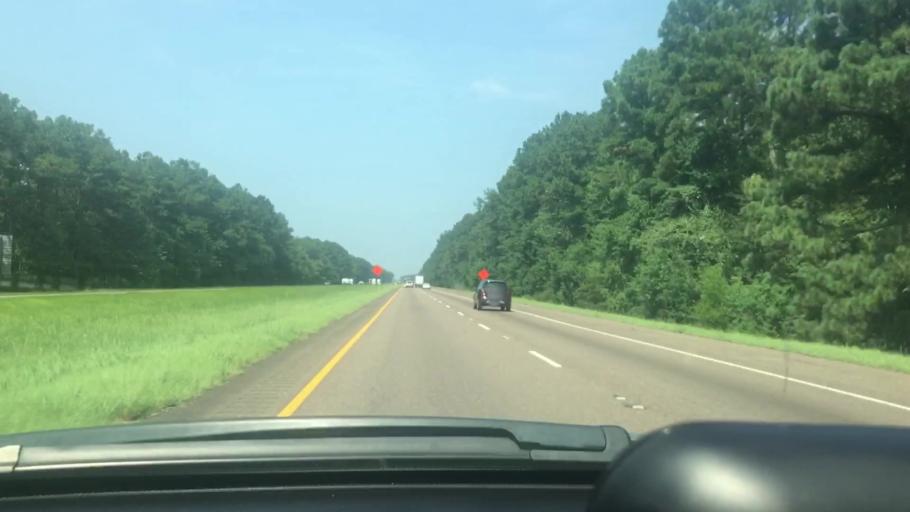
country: US
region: Louisiana
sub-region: Livingston Parish
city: Livingston
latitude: 30.4742
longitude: -90.7671
